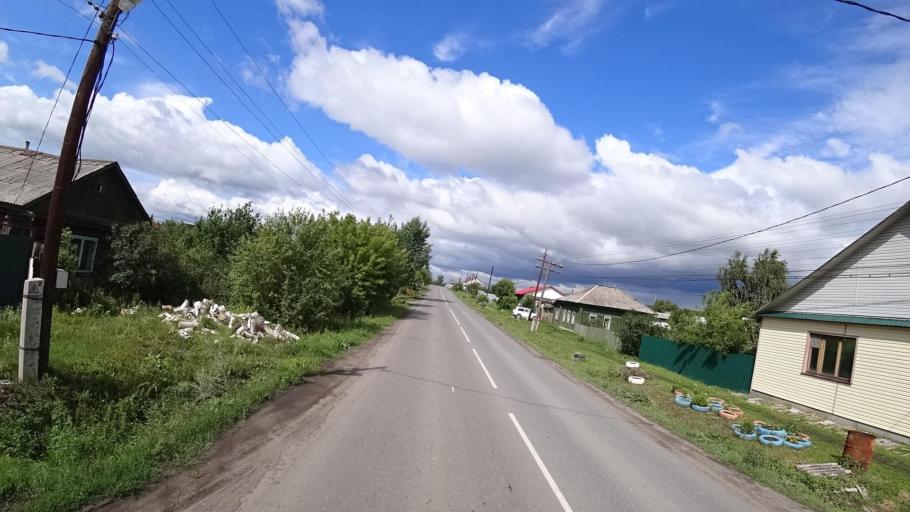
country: RU
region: Sverdlovsk
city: Kamyshlov
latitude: 56.8617
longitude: 62.7087
